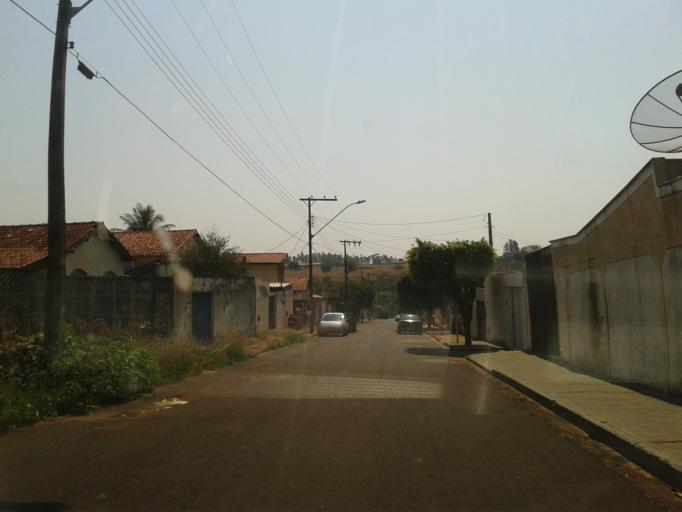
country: BR
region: Minas Gerais
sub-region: Ituiutaba
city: Ituiutaba
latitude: -18.9705
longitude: -49.4801
